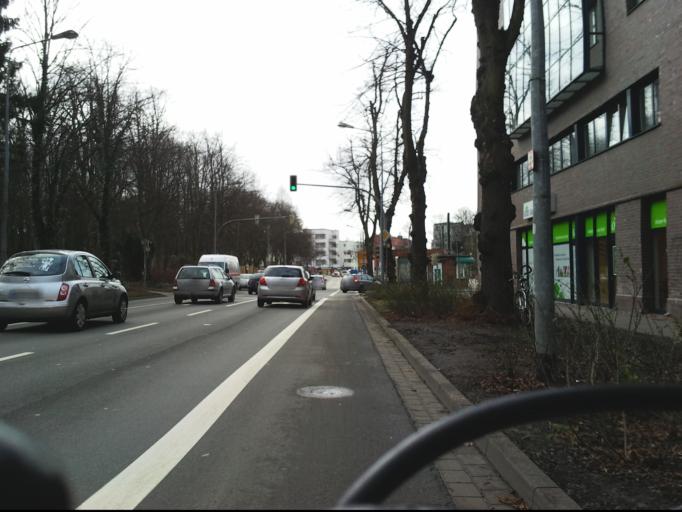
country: DE
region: Mecklenburg-Vorpommern
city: Rostock
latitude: 54.0856
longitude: 12.1188
